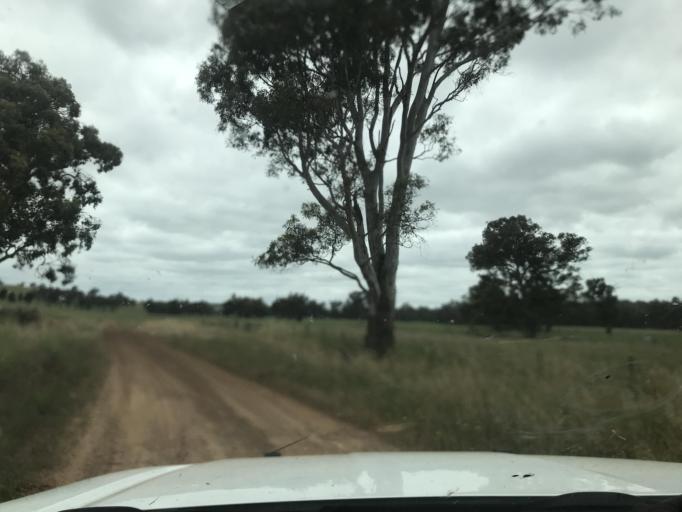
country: AU
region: South Australia
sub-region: Wattle Range
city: Penola
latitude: -37.3584
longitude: 141.2127
